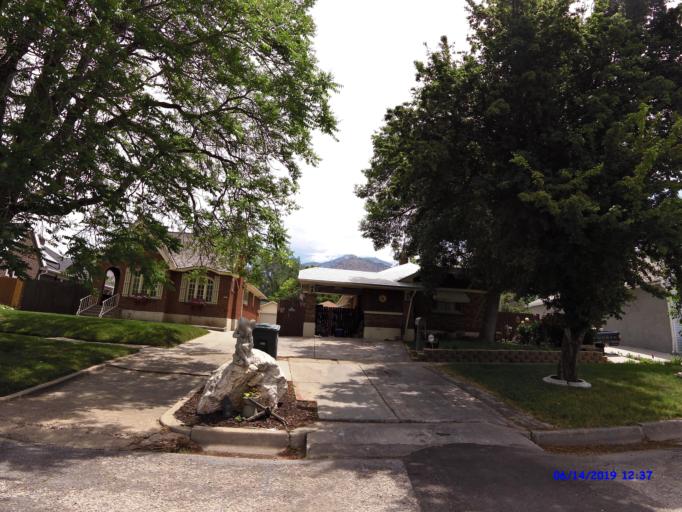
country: US
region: Utah
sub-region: Weber County
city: Ogden
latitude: 41.2106
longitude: -111.9540
